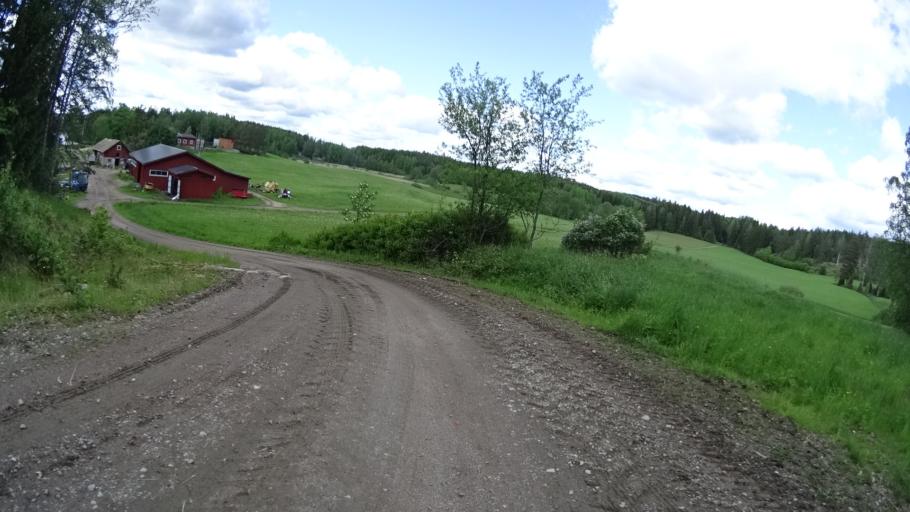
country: FI
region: Uusimaa
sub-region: Raaseporin
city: Karis
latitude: 60.1455
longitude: 23.6204
